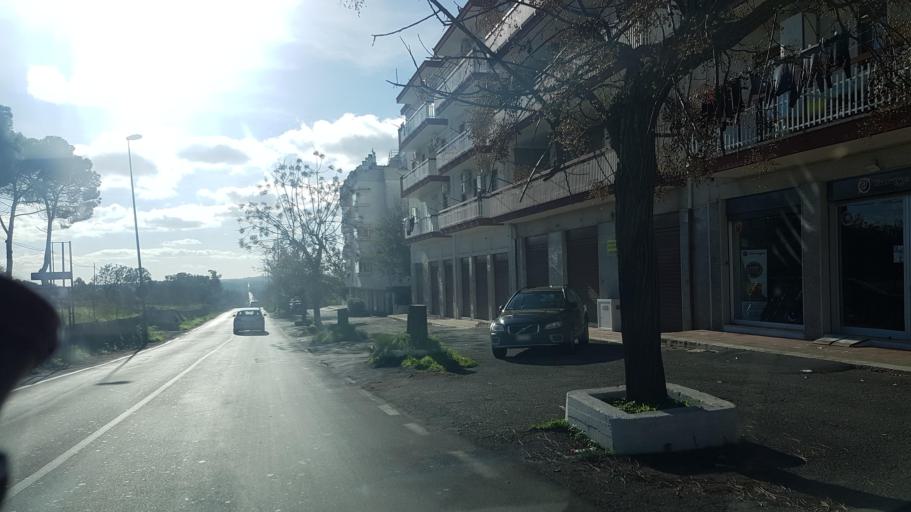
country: IT
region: Apulia
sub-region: Provincia di Brindisi
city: Ostuni
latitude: 40.7205
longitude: 17.5763
